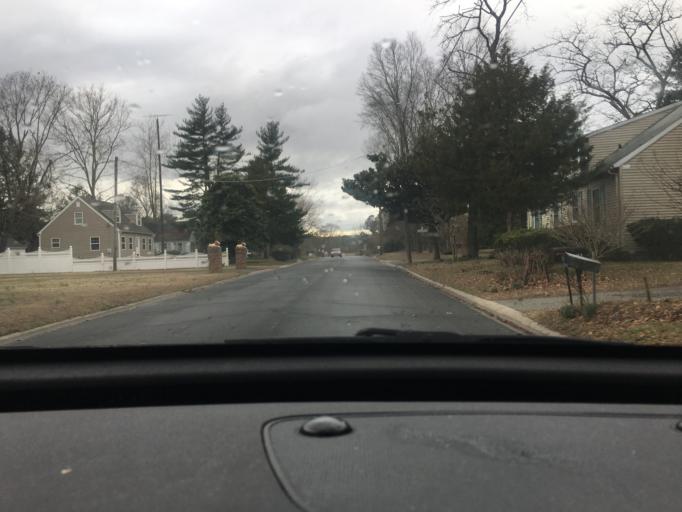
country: US
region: Maryland
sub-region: Wicomico County
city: Salisbury
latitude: 38.3799
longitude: -75.6167
